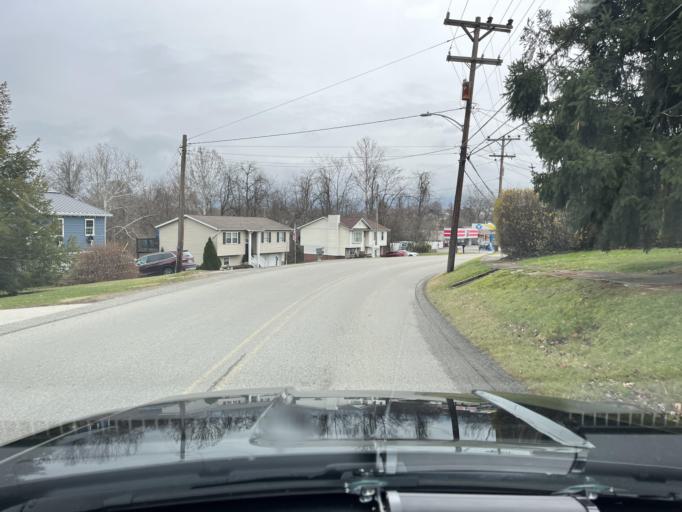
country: US
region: Pennsylvania
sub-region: Fayette County
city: South Uniontown
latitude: 39.8952
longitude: -79.7440
